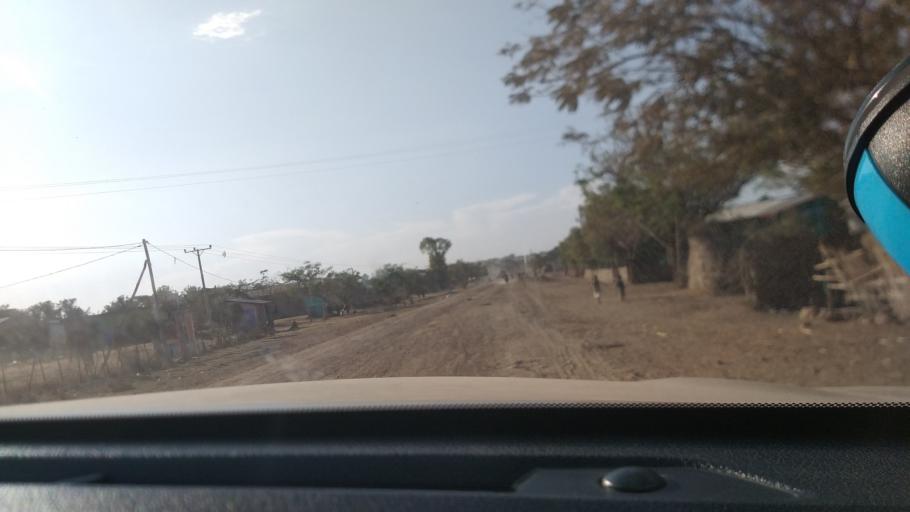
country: ET
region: Oromiya
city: Shashemene
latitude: 7.4892
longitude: 38.7210
